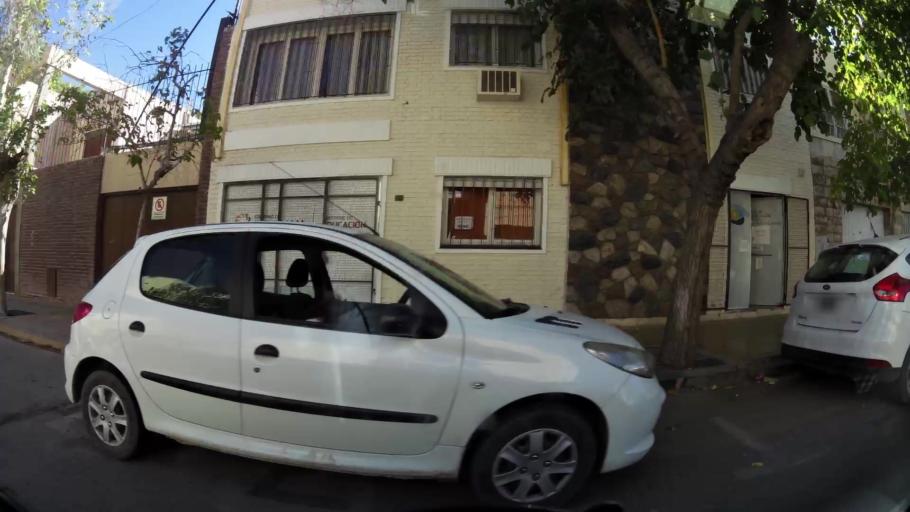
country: AR
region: San Juan
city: San Juan
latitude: -31.5358
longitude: -68.5352
